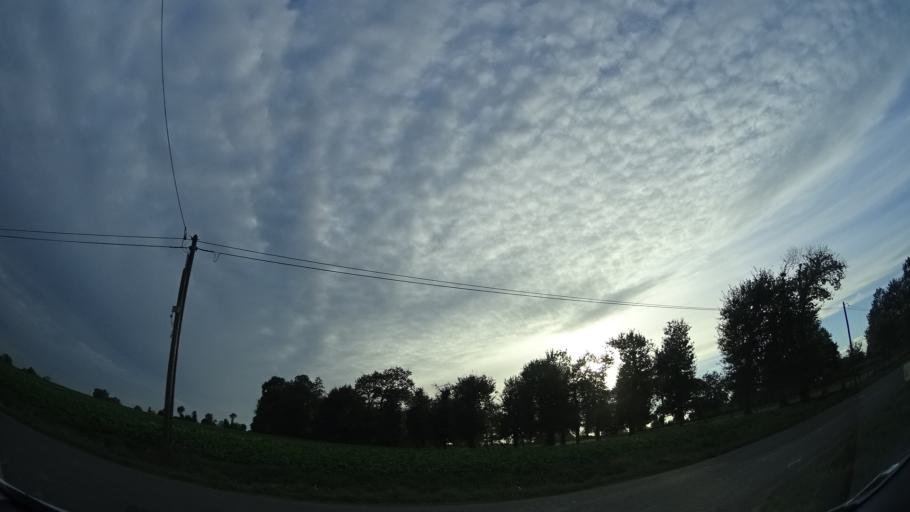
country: FR
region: Brittany
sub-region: Departement d'Ille-et-Vilaine
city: Geveze
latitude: 48.1890
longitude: -1.8063
